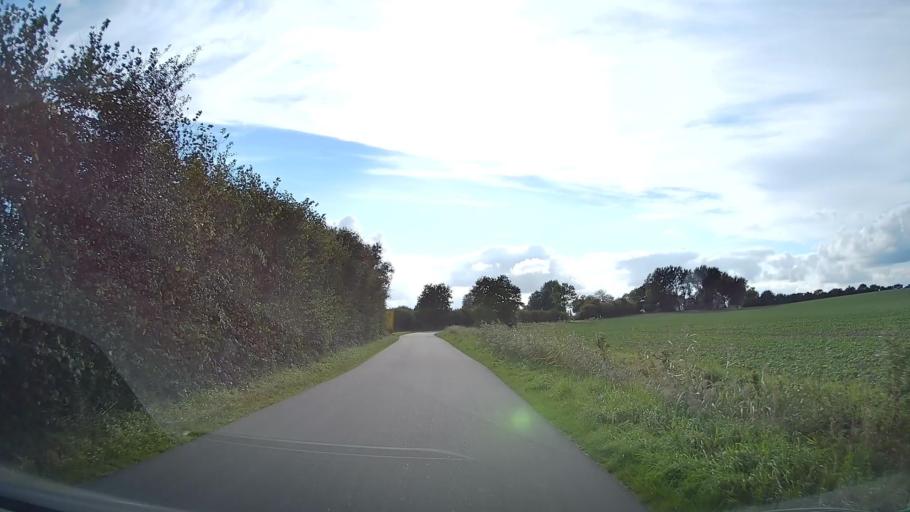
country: DE
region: Schleswig-Holstein
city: Pommerby
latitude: 54.7678
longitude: 9.9544
